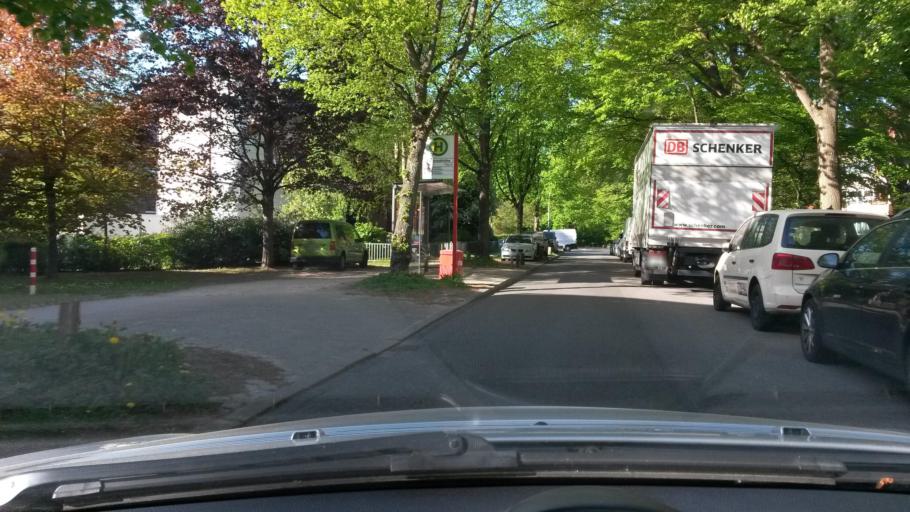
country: DE
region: Hamburg
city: Farmsen-Berne
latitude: 53.6214
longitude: 10.1300
